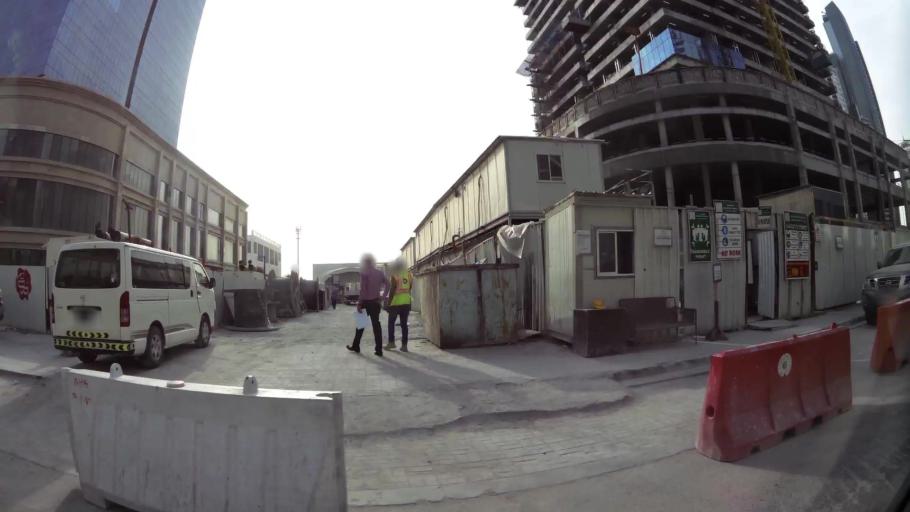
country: QA
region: Baladiyat ad Dawhah
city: Doha
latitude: 25.3229
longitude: 51.5261
